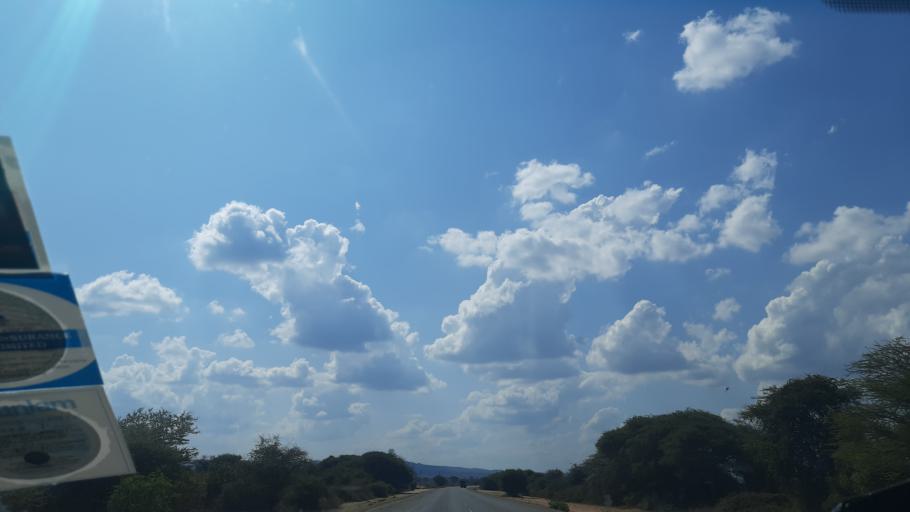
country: TZ
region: Singida
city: Kilimatinde
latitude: -5.8348
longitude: 35.0638
